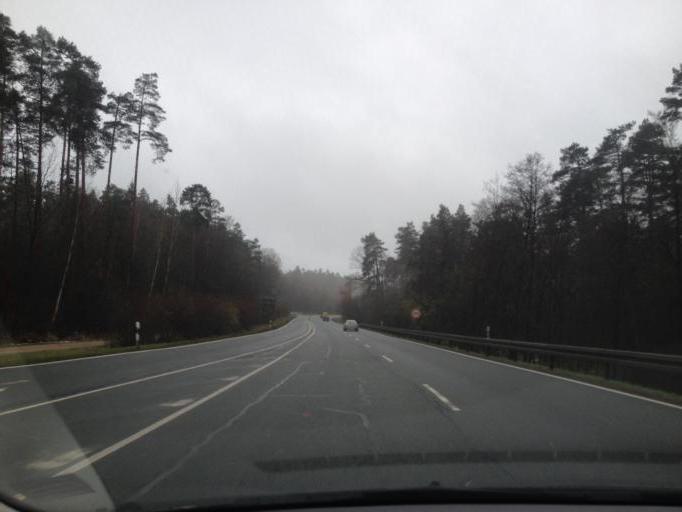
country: DE
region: Bavaria
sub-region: Regierungsbezirk Mittelfranken
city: Heroldsberg
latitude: 49.5195
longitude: 11.1484
